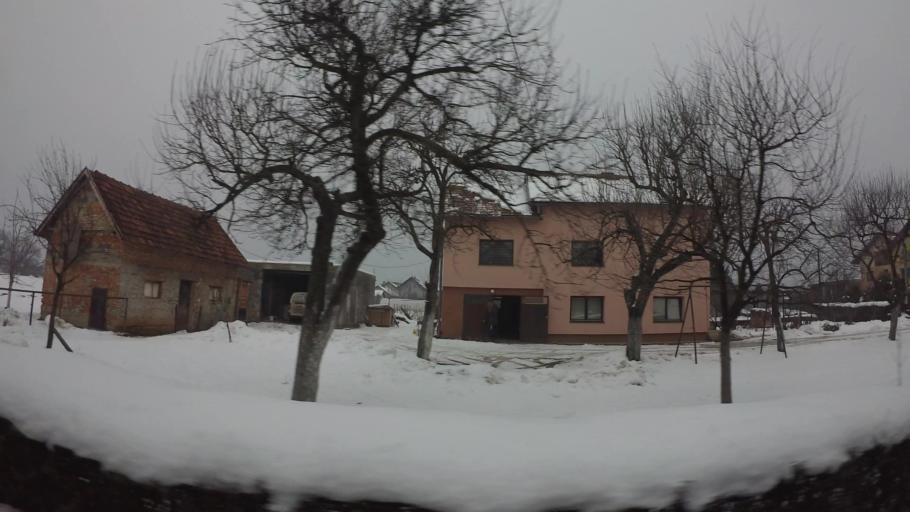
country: BA
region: Federation of Bosnia and Herzegovina
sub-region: Kanton Sarajevo
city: Sarajevo
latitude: 43.8394
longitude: 18.3073
